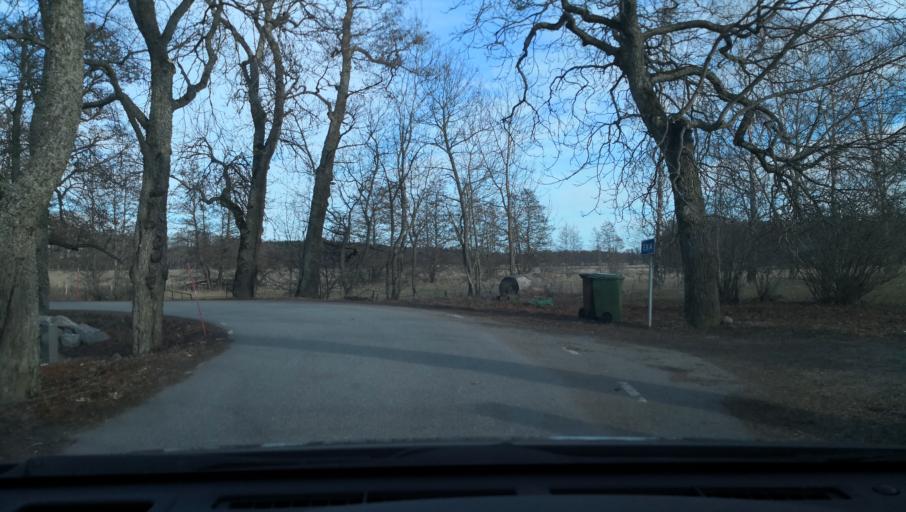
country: SE
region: Uppsala
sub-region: Enkopings Kommun
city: Grillby
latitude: 59.5419
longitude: 17.2014
